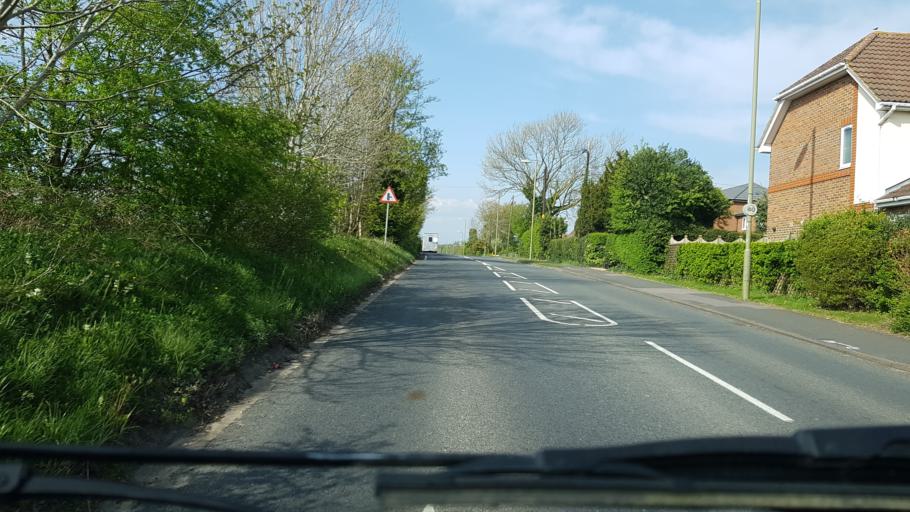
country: GB
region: England
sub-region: Hampshire
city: Basingstoke
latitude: 51.2666
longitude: -1.1322
